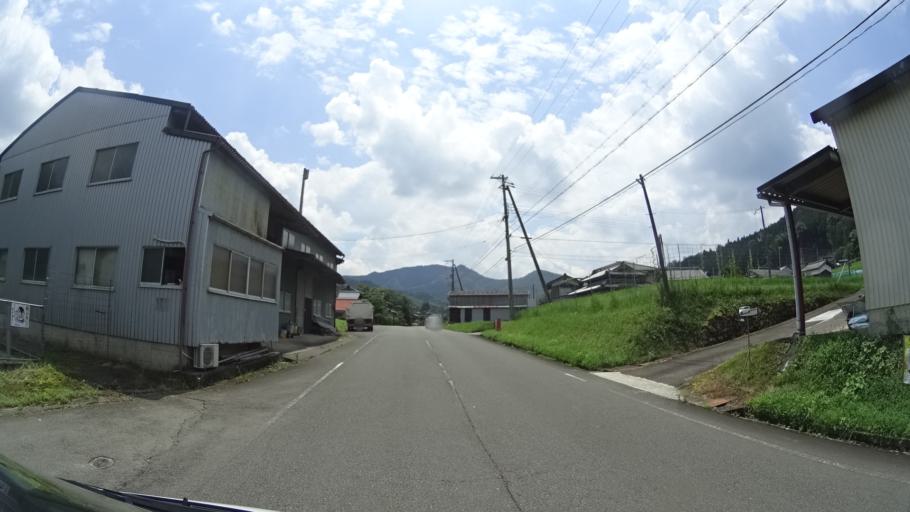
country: JP
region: Kyoto
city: Ayabe
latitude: 35.1822
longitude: 135.2781
